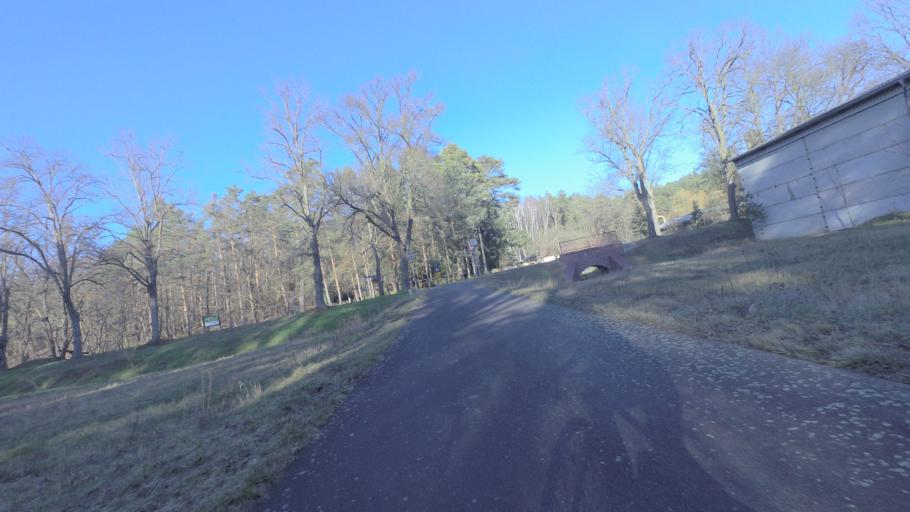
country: DE
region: Brandenburg
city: Ihlow
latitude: 52.0009
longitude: 13.3306
